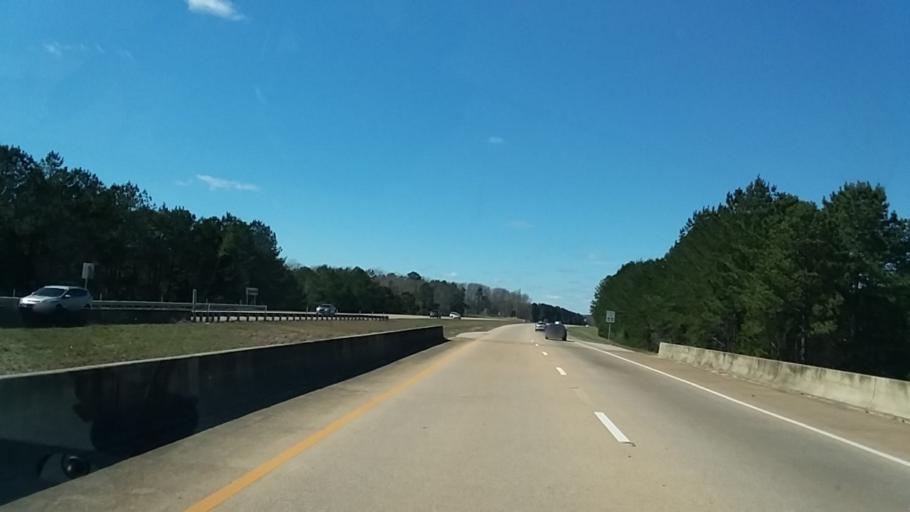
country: US
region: Mississippi
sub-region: Alcorn County
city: Farmington
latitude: 34.8815
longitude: -88.4469
